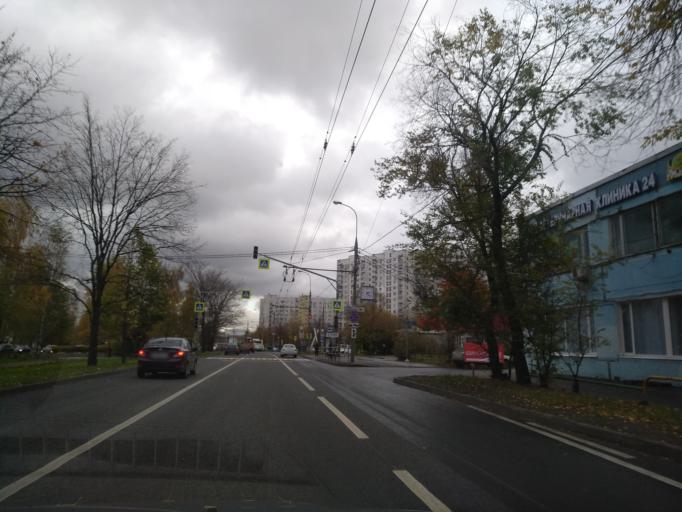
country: RU
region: Moscow
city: Bibirevo
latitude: 55.8918
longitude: 37.6189
